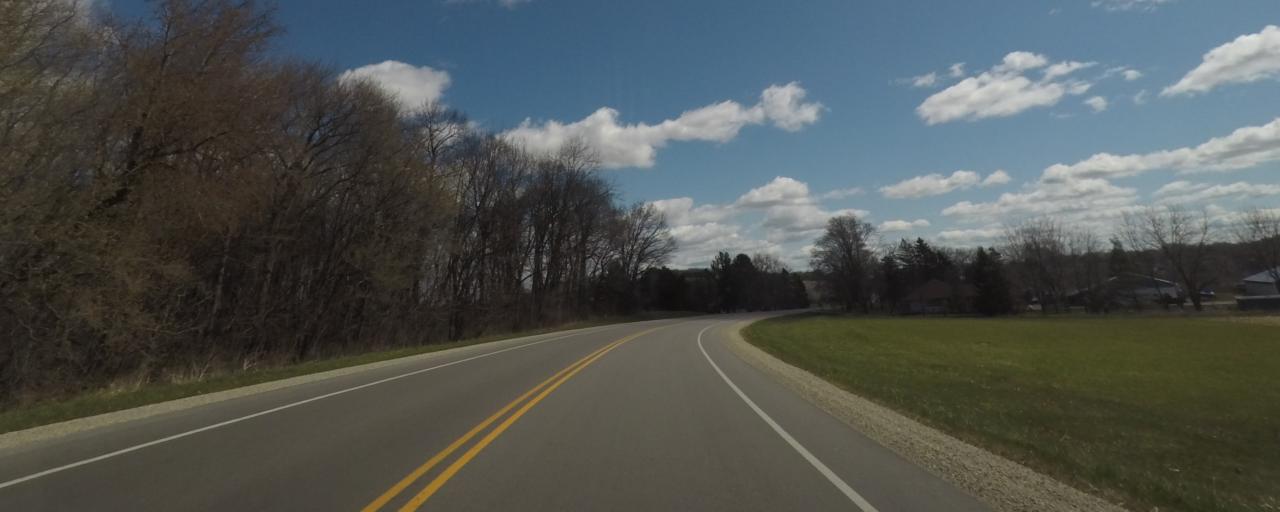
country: US
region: Wisconsin
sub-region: Jefferson County
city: Lake Mills
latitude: 43.0907
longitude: -88.9520
